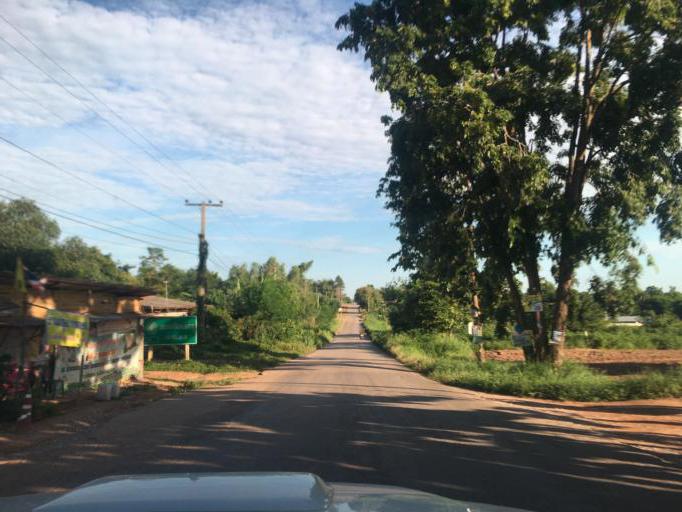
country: TH
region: Changwat Udon Thani
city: Kut Chap
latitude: 17.3053
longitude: 102.6689
